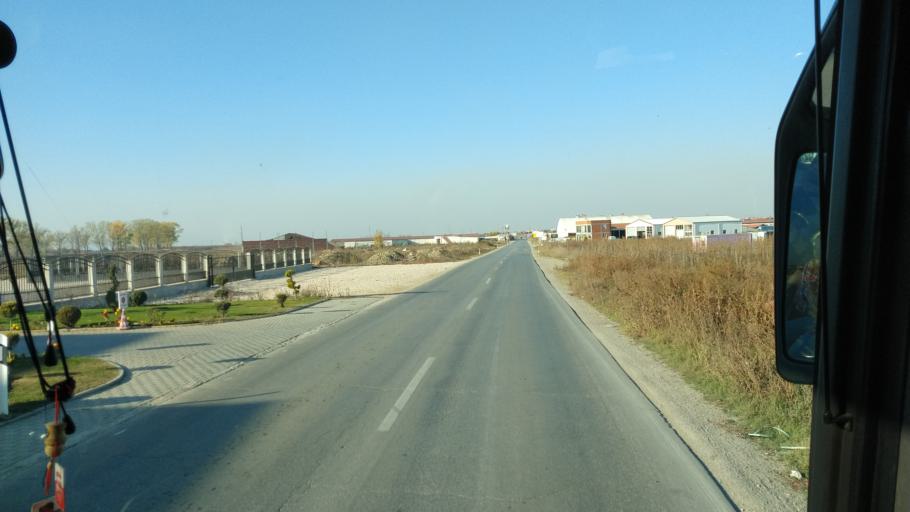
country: XK
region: Pristina
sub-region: Lipjan
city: Lipljan
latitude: 42.5162
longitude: 21.1127
